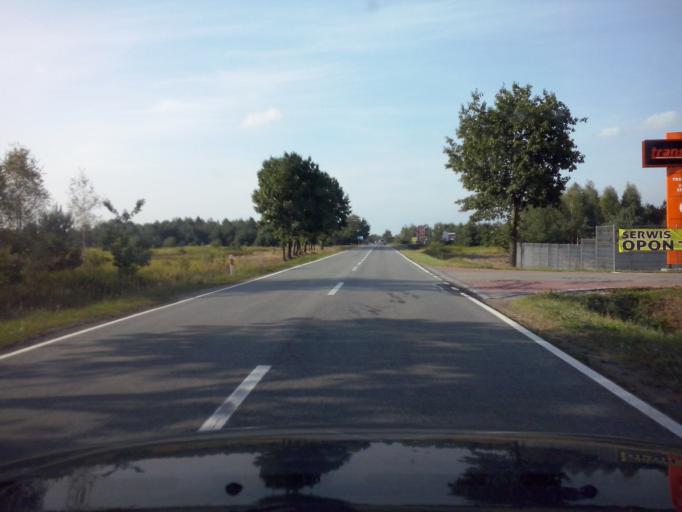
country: PL
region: Subcarpathian Voivodeship
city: Nowa Sarzyna
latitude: 50.3483
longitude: 22.3245
